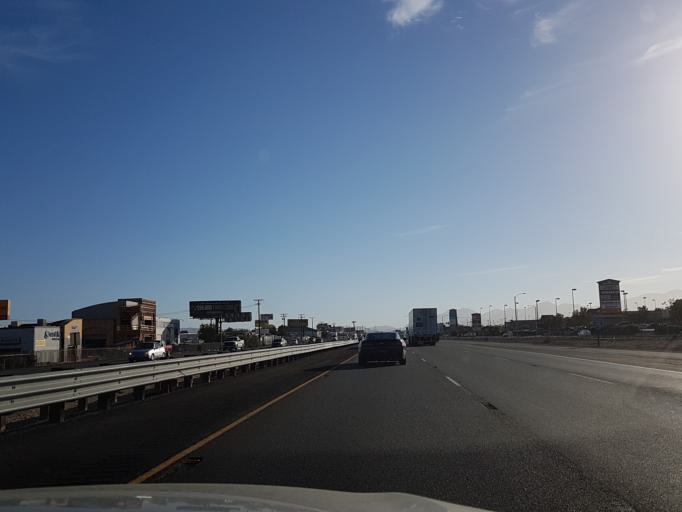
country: US
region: California
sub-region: San Bernardino County
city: Mountain View Acres
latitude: 34.4686
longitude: -117.3477
